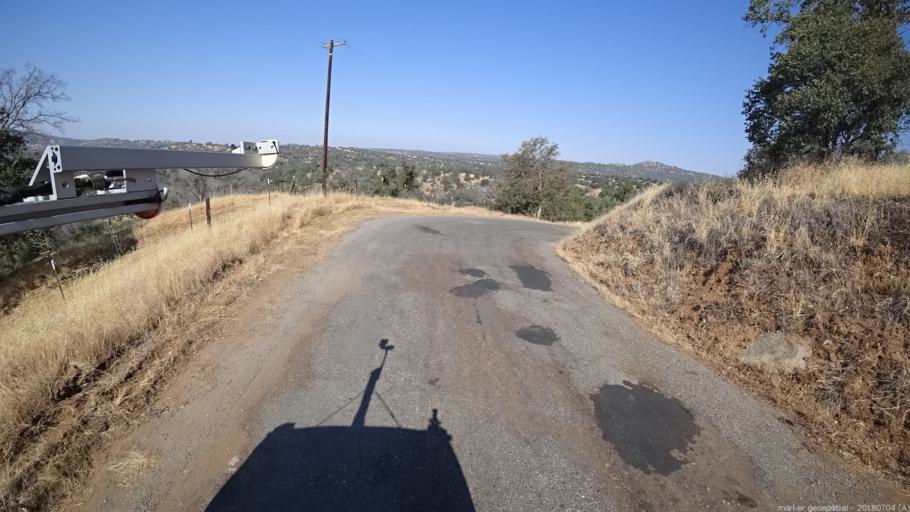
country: US
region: California
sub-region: Fresno County
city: Auberry
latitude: 37.1075
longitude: -119.6317
